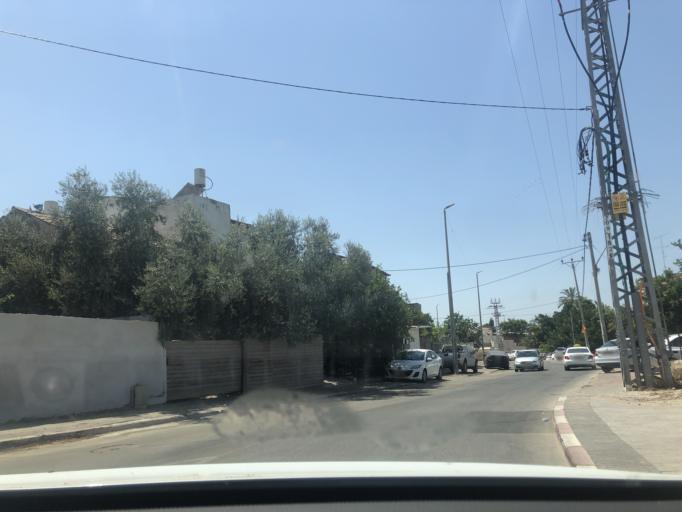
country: IL
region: Central District
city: Lod
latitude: 31.9562
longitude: 34.9032
